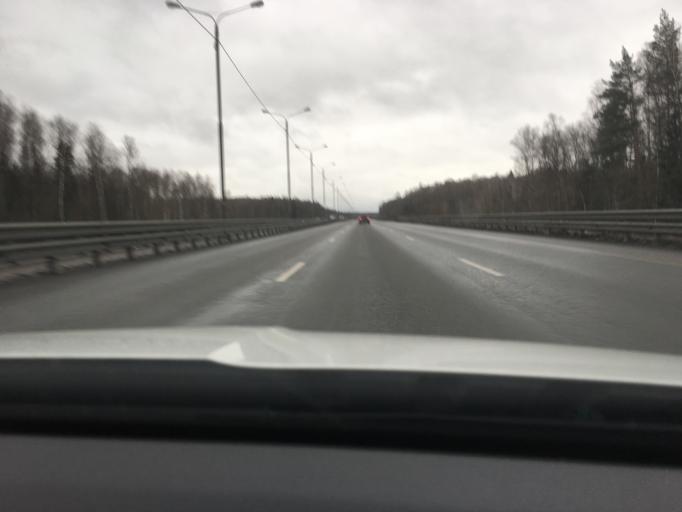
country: RU
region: Moskovskaya
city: Novyy Byt
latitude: 55.1216
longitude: 37.5727
